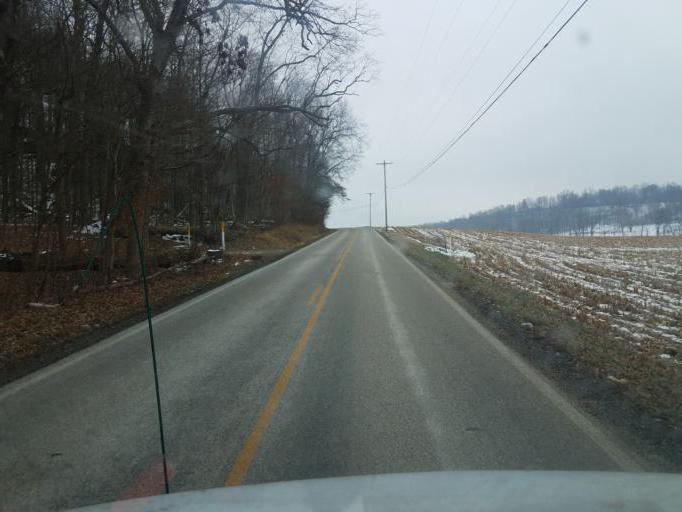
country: US
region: Ohio
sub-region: Sandusky County
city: Bellville
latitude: 40.6606
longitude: -82.4109
